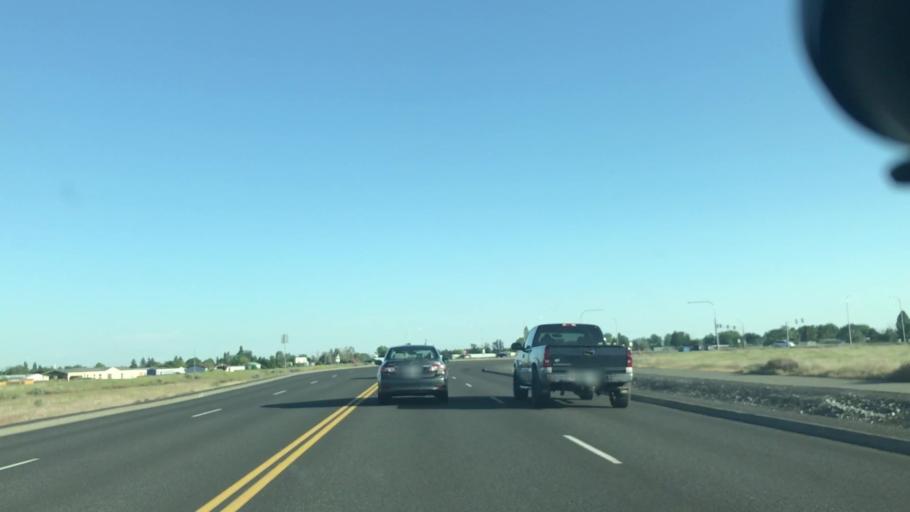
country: US
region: Washington
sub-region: Grant County
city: Cascade Valley
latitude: 47.1581
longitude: -119.3118
